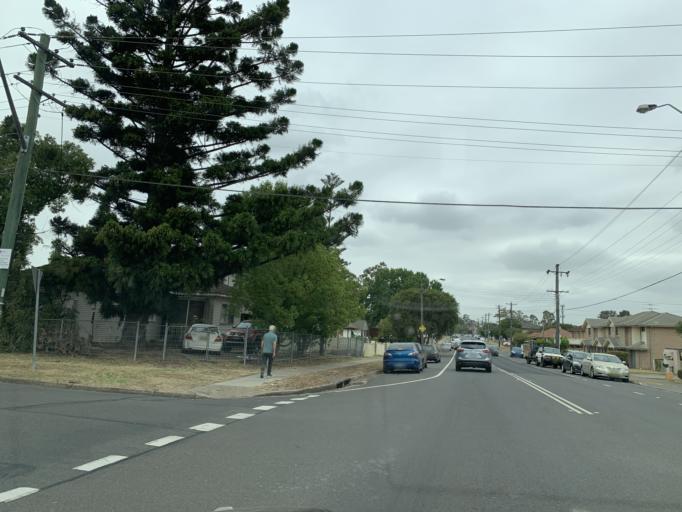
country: AU
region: New South Wales
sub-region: Blacktown
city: Doonside
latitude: -33.7586
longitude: 150.8704
